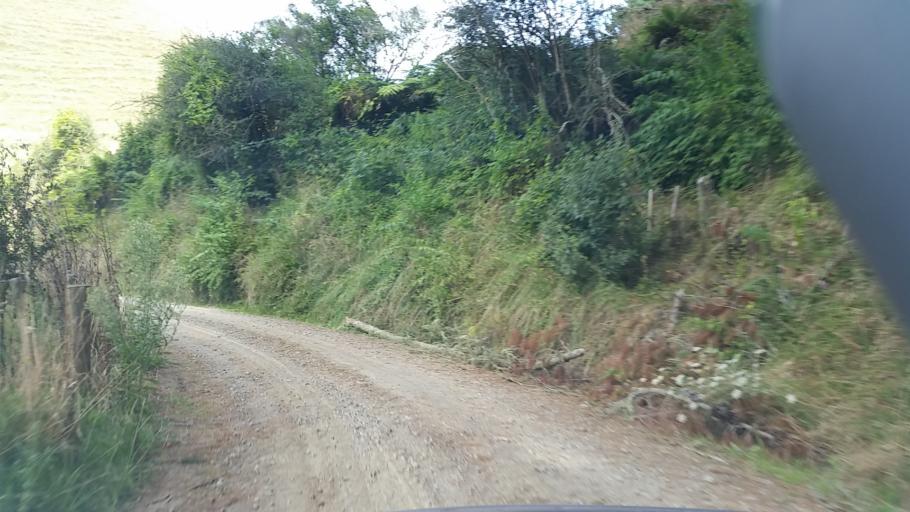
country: NZ
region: Taranaki
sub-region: South Taranaki District
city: Eltham
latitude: -39.2530
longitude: 174.5665
